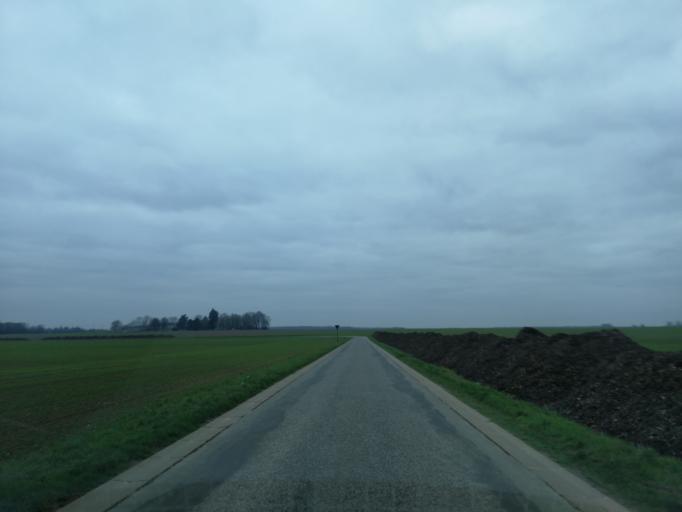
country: FR
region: Ile-de-France
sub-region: Departement de l'Essonne
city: Limours
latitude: 48.6624
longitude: 2.0925
